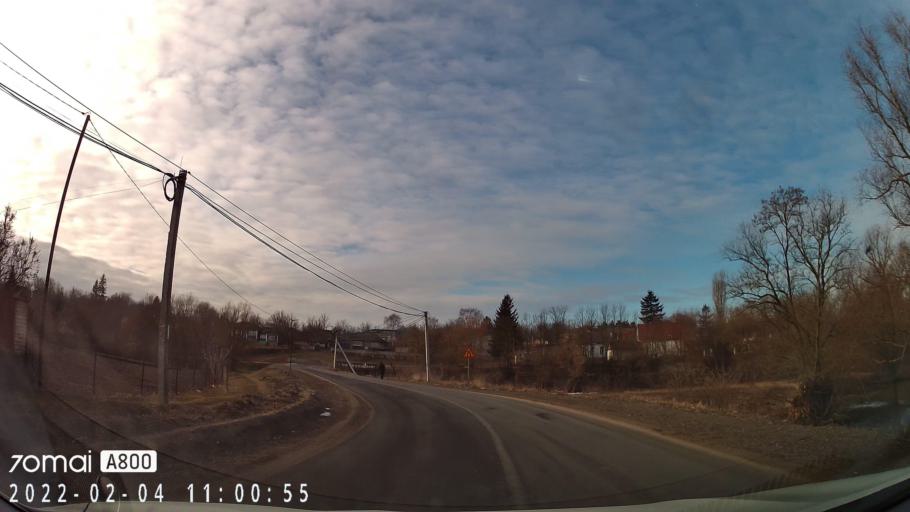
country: RO
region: Botosani
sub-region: Comuna Radauti-Prut
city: Miorcani
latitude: 48.2970
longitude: 26.9380
